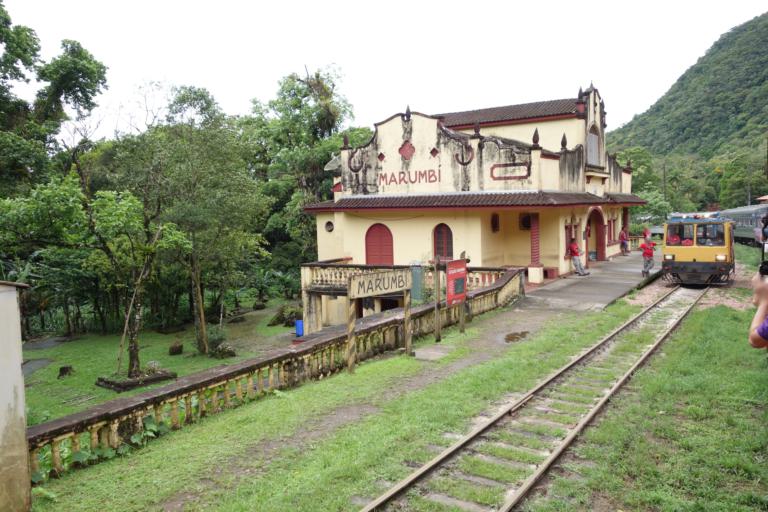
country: BR
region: Parana
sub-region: Piraquara
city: Piraquara
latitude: -25.4482
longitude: -48.8924
